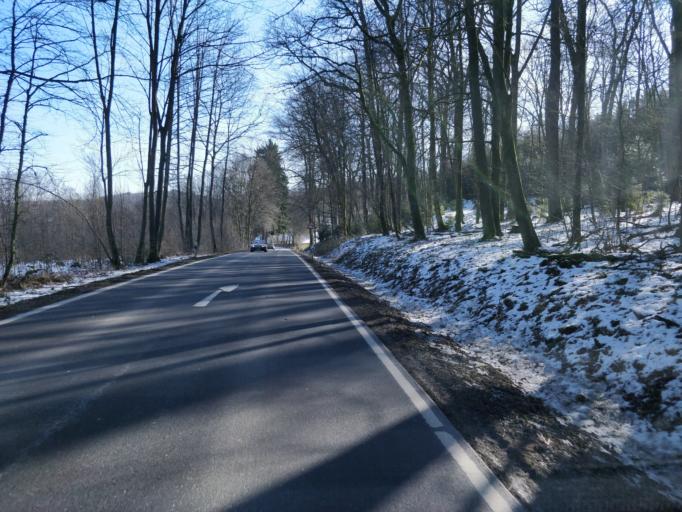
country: DE
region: North Rhine-Westphalia
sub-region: Regierungsbezirk Koln
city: Numbrecht
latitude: 50.9194
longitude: 7.5533
